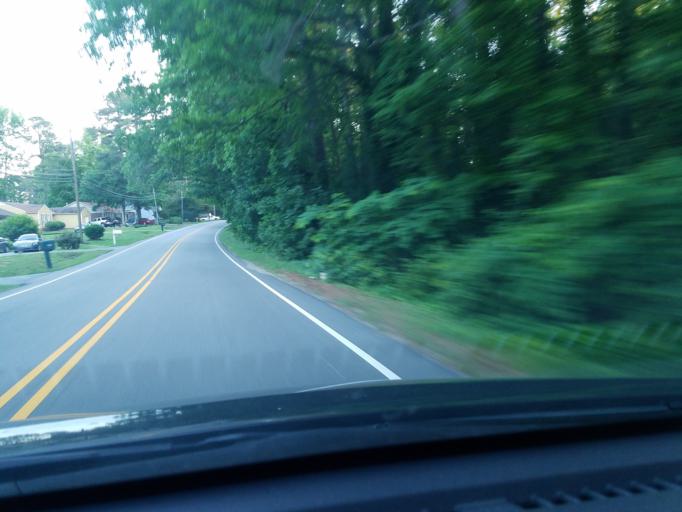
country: US
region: North Carolina
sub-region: Durham County
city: Durham
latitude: 35.9553
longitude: -78.9355
